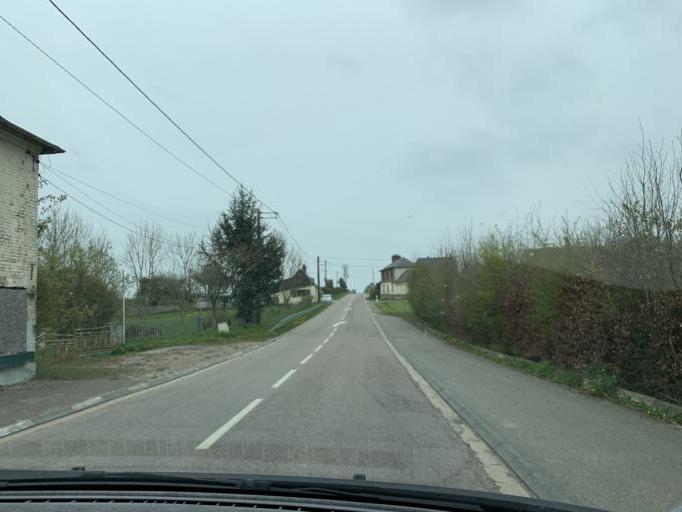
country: FR
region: Haute-Normandie
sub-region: Departement de la Seine-Maritime
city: Foucarmont
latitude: 49.8324
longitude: 1.5192
